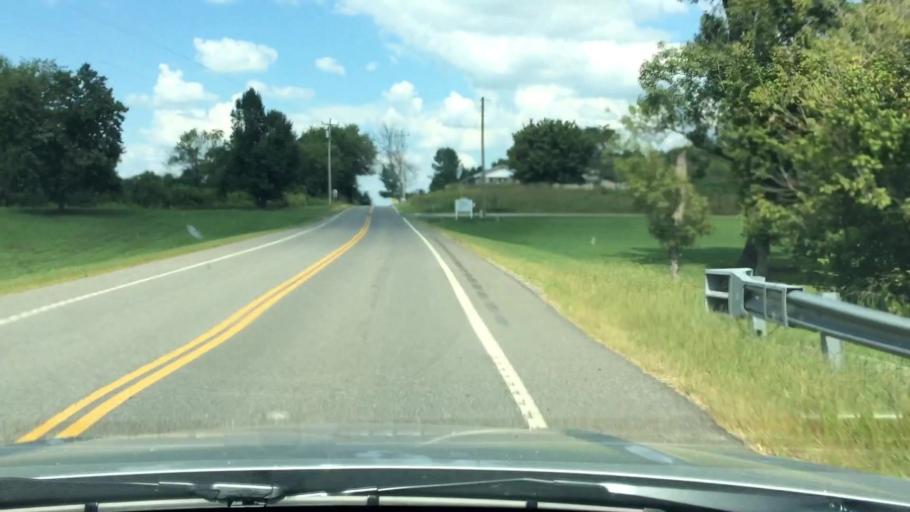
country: US
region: Tennessee
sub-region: McMinn County
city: Englewood
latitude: 35.4916
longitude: -84.5085
